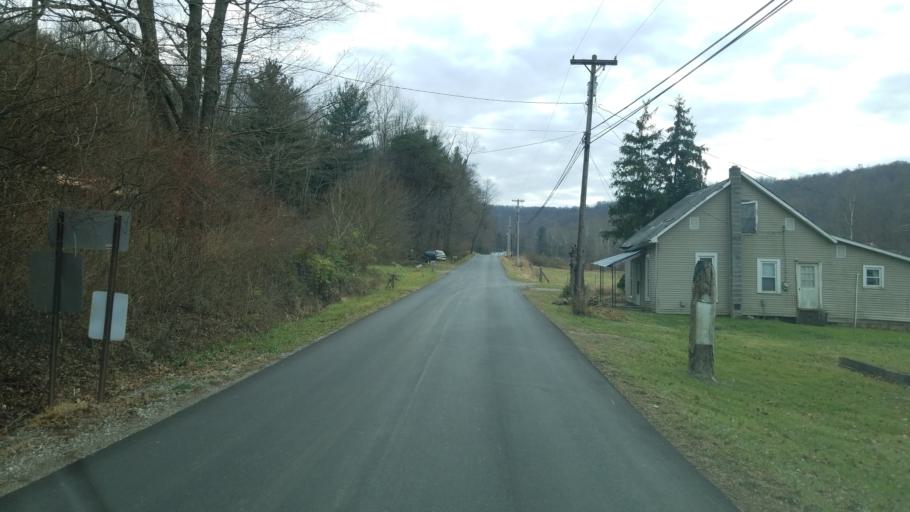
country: US
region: Ohio
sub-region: Highland County
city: Greenfield
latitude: 39.2200
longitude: -83.2687
